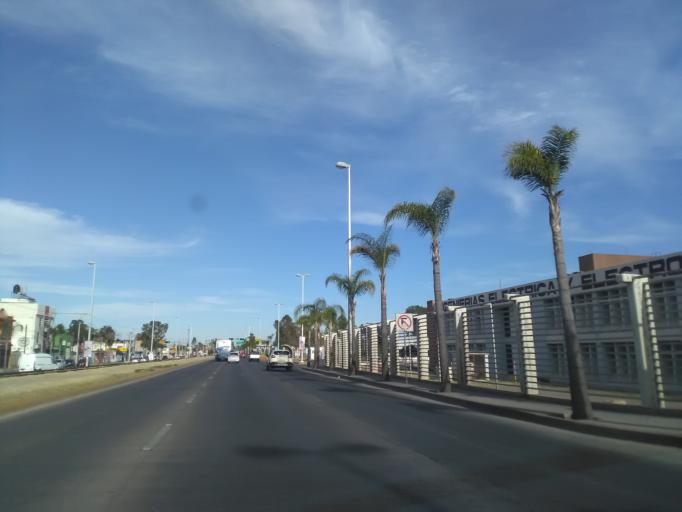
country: MX
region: Durango
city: Victoria de Durango
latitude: 24.0362
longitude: -104.6453
